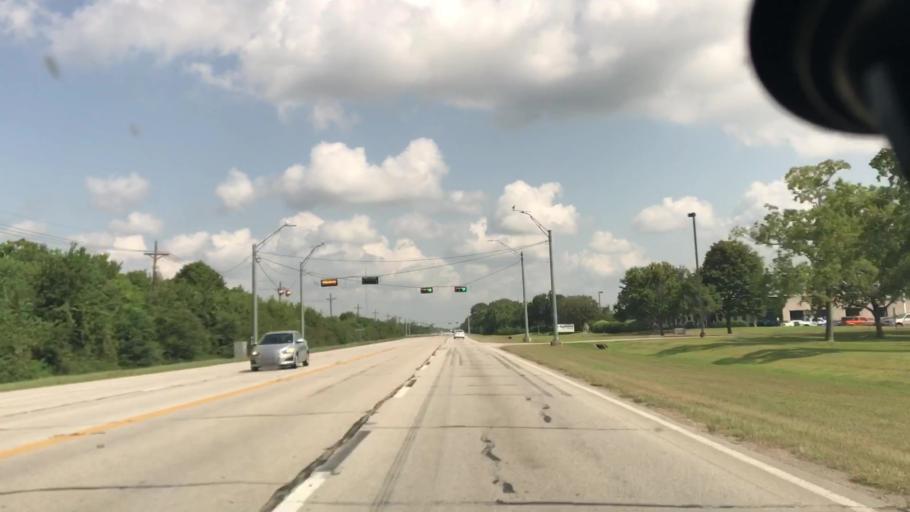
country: US
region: Texas
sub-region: Brazoria County
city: Angleton
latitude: 29.2049
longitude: -95.4355
